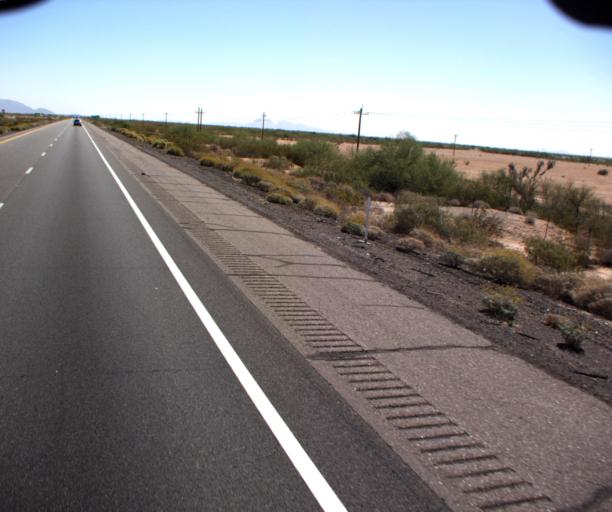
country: US
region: Arizona
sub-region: La Paz County
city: Salome
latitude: 33.5663
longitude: -113.3371
